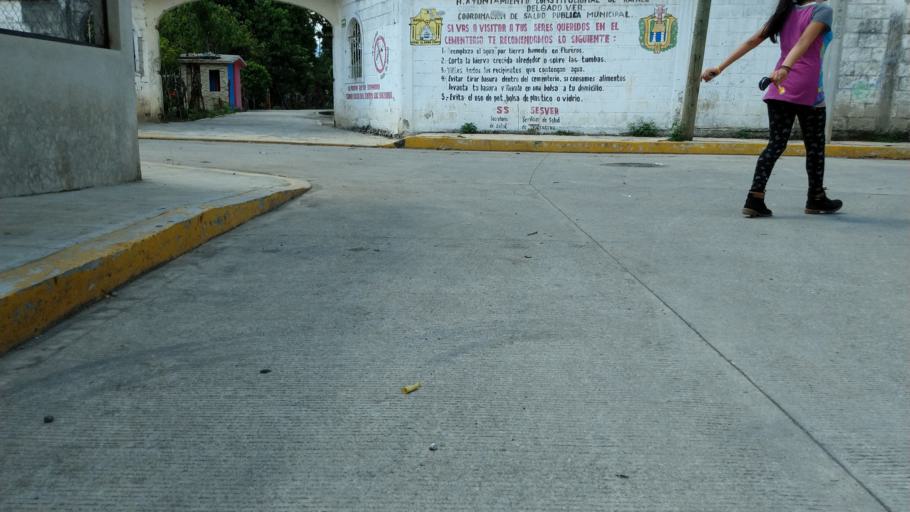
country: MX
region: Veracruz
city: Jalapilla
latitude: 18.8143
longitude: -97.0661
